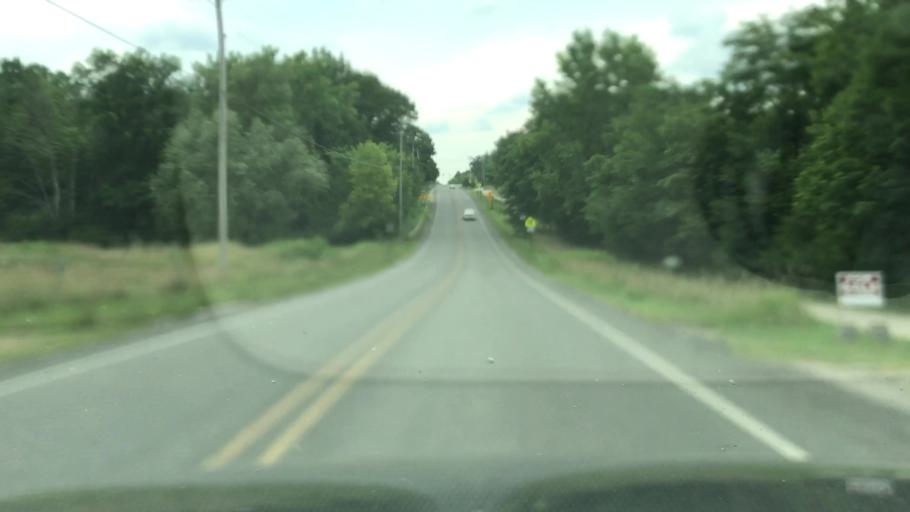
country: US
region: Michigan
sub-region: Kent County
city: East Grand Rapids
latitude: 42.9847
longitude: -85.5697
